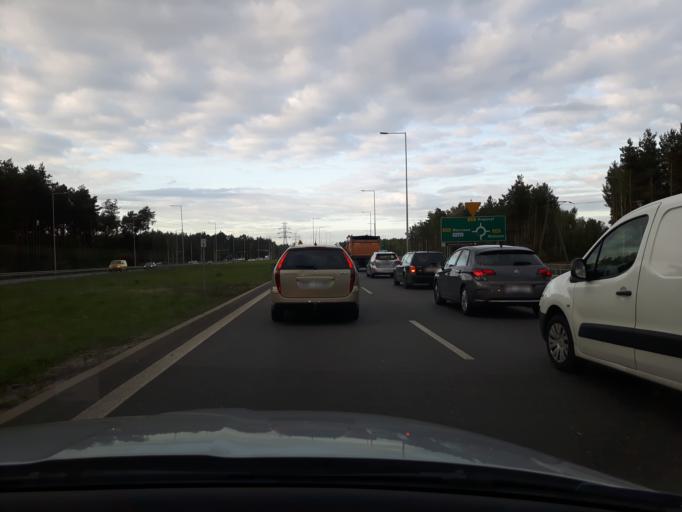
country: PL
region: Masovian Voivodeship
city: Zielonka
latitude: 52.2918
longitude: 21.1390
